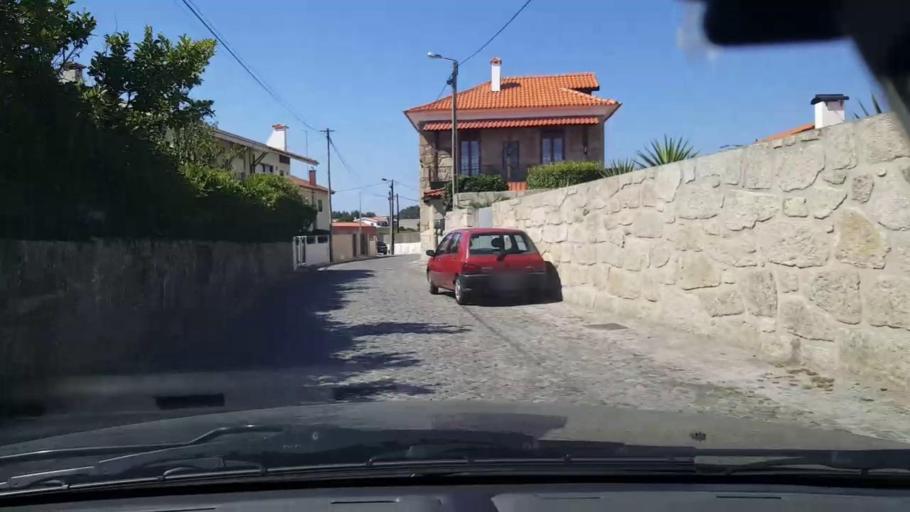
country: PT
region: Porto
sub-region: Matosinhos
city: Lavra
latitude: 41.2943
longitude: -8.7209
